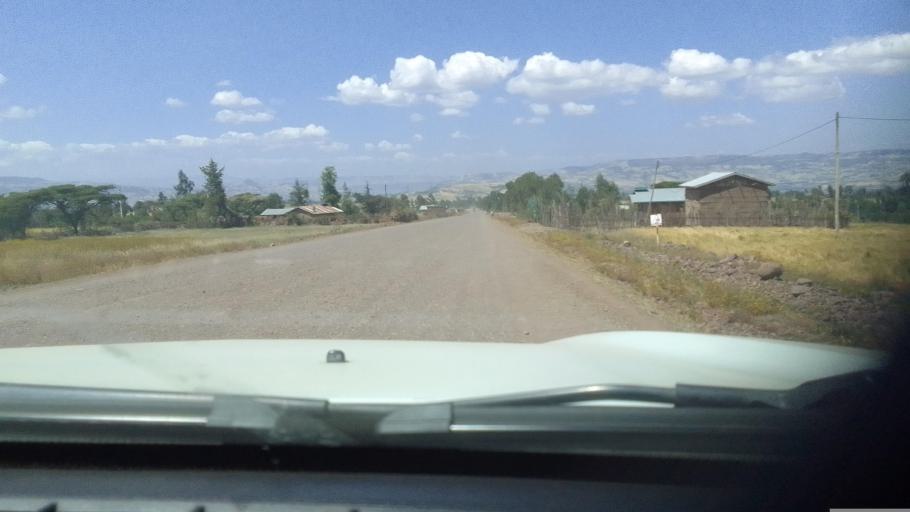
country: ET
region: Oromiya
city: Hagere Hiywet
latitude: 8.9270
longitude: 37.8610
